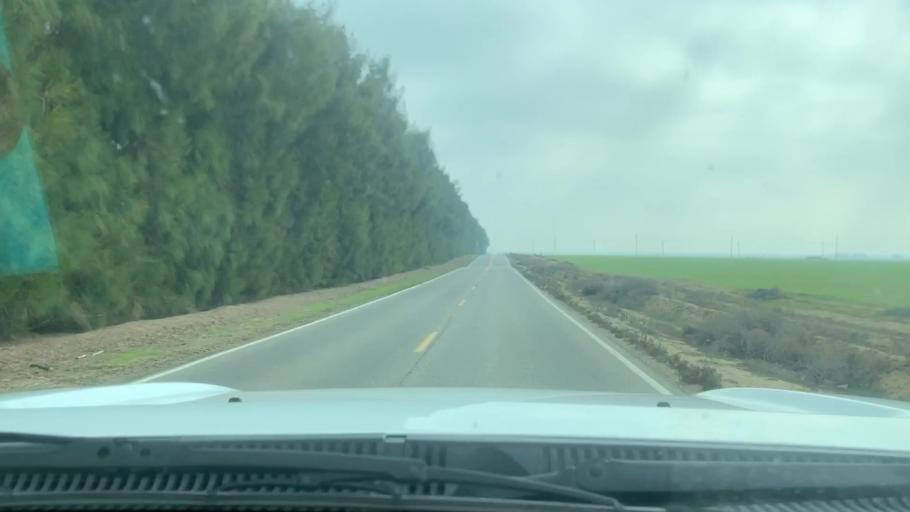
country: US
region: California
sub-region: Kern County
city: Lost Hills
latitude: 35.5048
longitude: -119.7438
